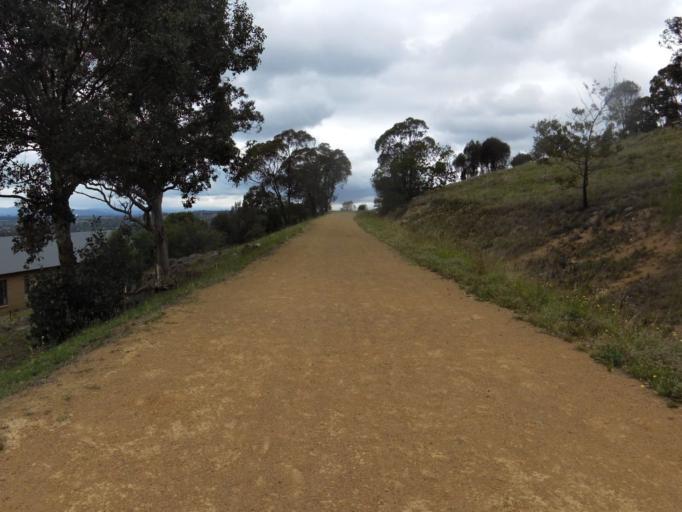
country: AU
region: Australian Capital Territory
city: Forrest
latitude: -35.3538
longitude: 149.0279
